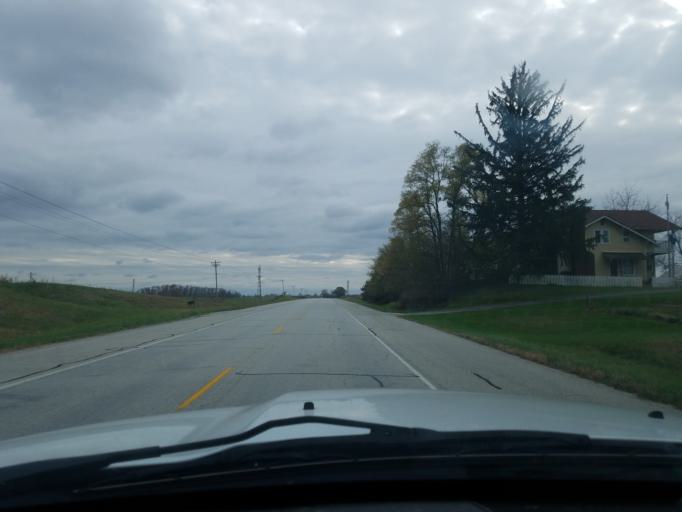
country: US
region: Indiana
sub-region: Bartholomew County
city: Hope
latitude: 39.1935
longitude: -85.7721
